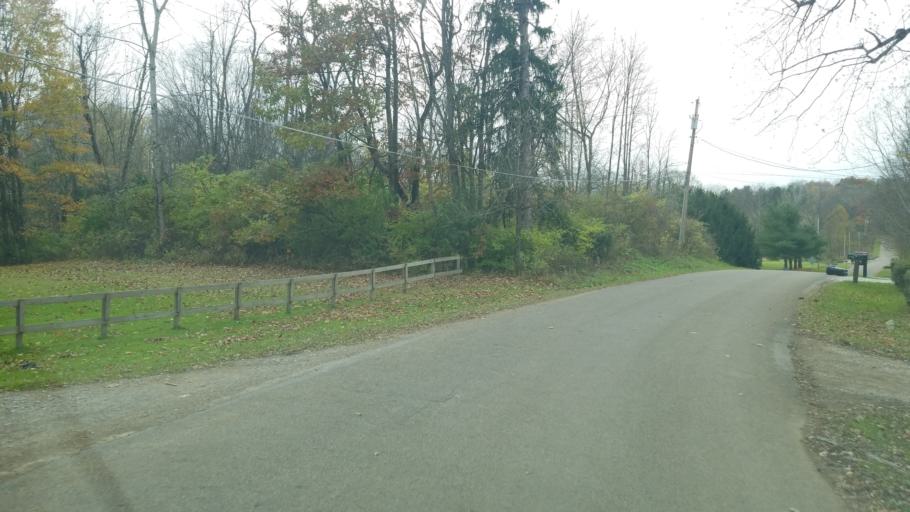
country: US
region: Ohio
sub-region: Richland County
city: Mansfield
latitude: 40.7263
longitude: -82.4839
